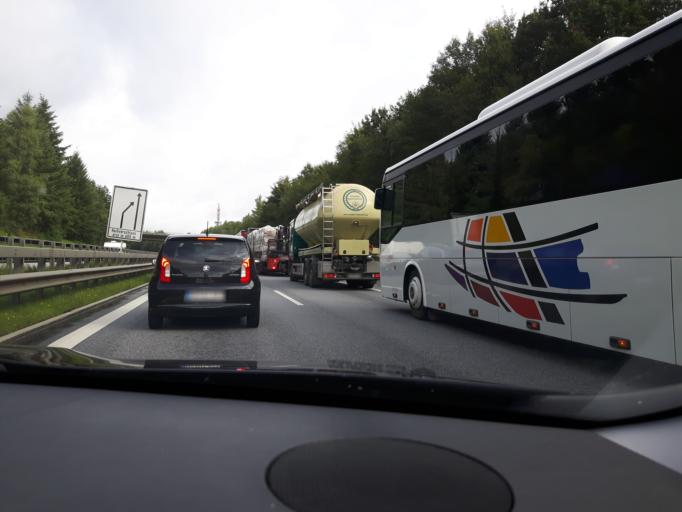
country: DE
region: Lower Saxony
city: Seevetal
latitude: 53.4295
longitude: 9.9283
